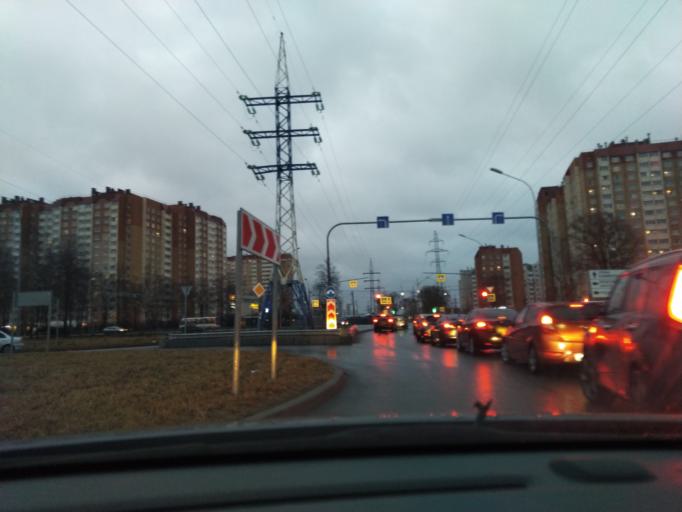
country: RU
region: St.-Petersburg
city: Gorelovo
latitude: 59.7915
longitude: 30.1447
